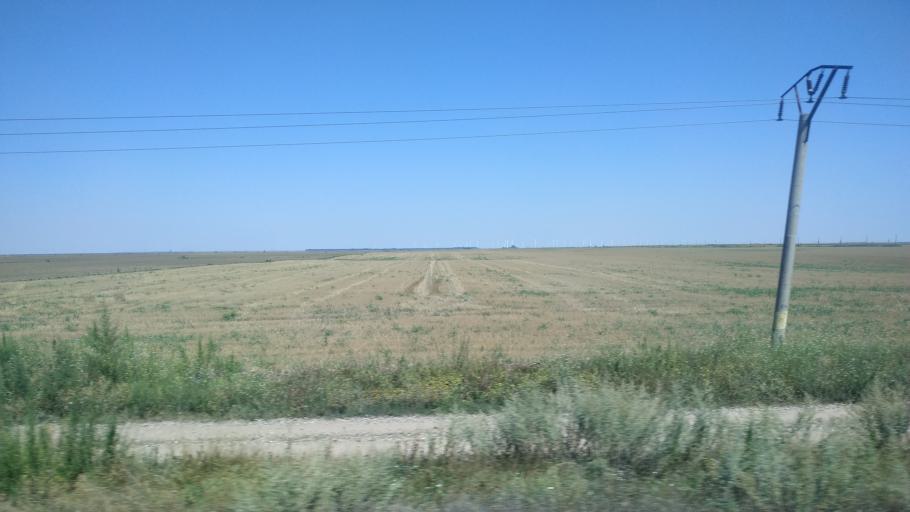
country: RO
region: Calarasi
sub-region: Comuna Borcea
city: Borcea
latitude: 44.4194
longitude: 27.7269
